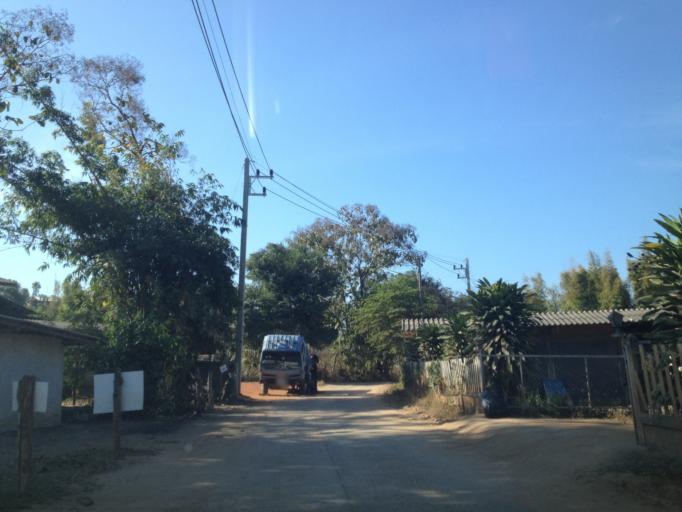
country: TH
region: Mae Hong Son
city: Ban Huai I Huak
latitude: 18.0828
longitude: 98.1941
